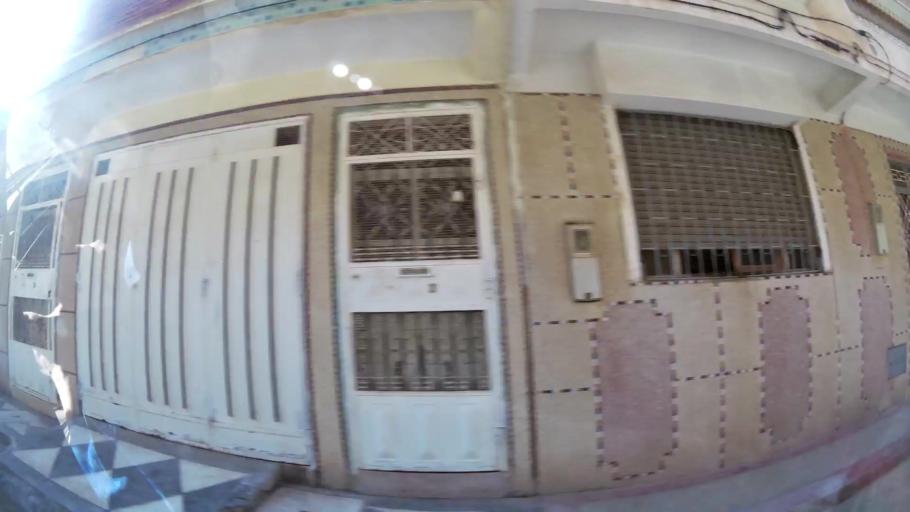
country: MA
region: Oriental
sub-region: Oujda-Angad
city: Oujda
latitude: 34.6761
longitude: -1.9059
